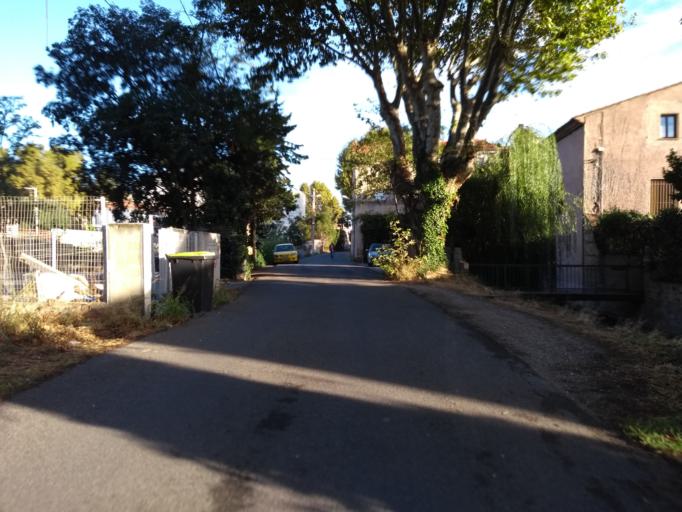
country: FR
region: Languedoc-Roussillon
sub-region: Departement des Pyrenees-Orientales
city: Perpignan
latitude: 42.7186
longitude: 2.8879
